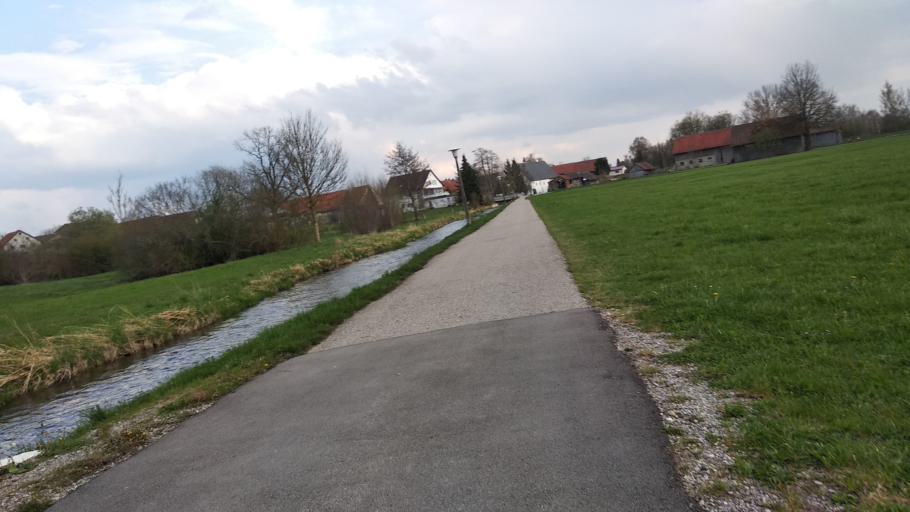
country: DE
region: Bavaria
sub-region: Swabia
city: Mindelheim
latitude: 48.0320
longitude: 10.4906
